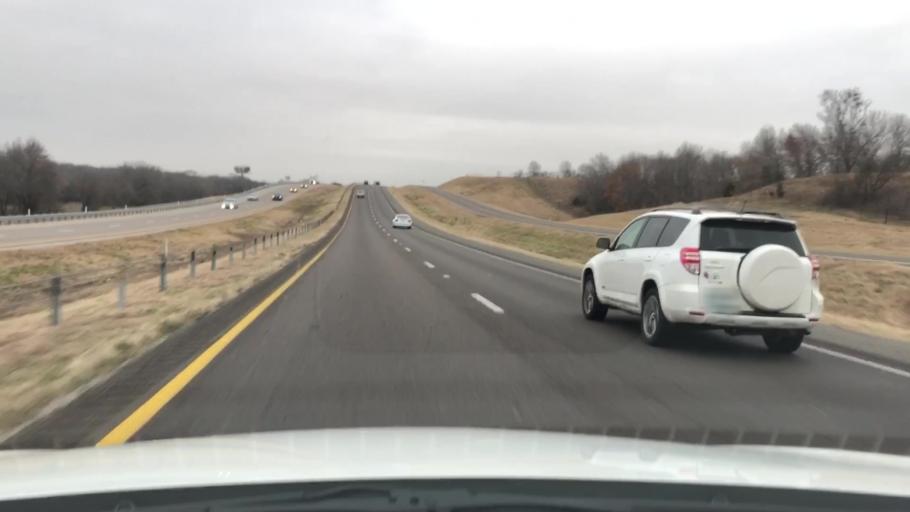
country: US
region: Texas
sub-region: Cooke County
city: Gainesville
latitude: 33.6995
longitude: -97.1626
